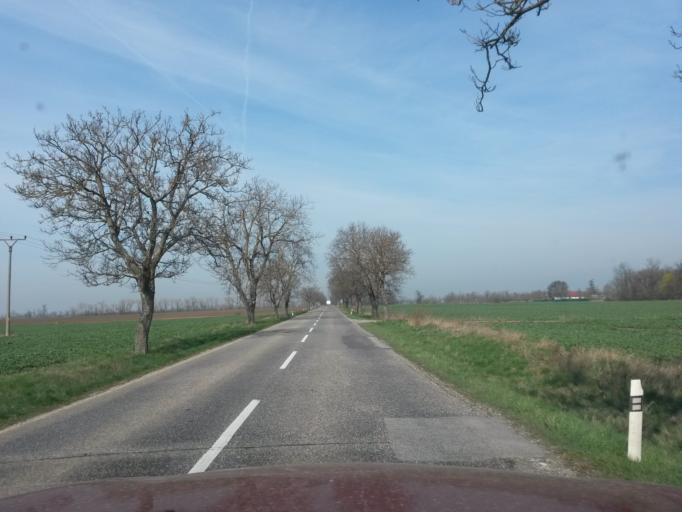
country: SK
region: Nitriansky
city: Levice
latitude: 48.1382
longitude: 18.5884
